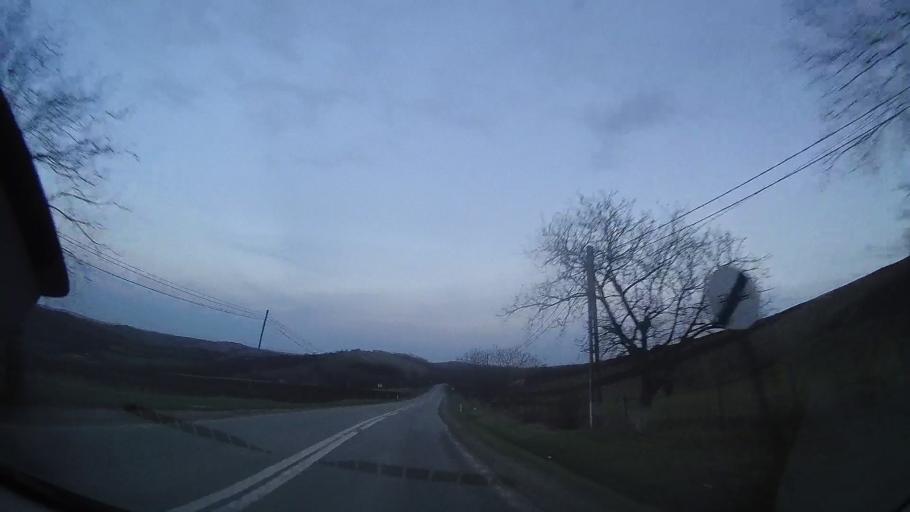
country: RO
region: Cluj
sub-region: Comuna Mociu
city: Mociu
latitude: 46.7975
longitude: 24.0113
